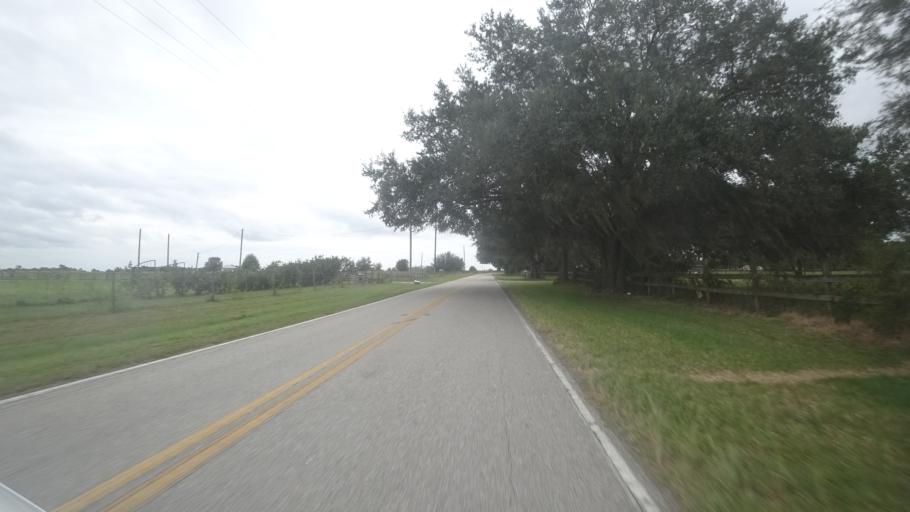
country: US
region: Florida
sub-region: Sarasota County
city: Lake Sarasota
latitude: 27.4013
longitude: -82.1309
